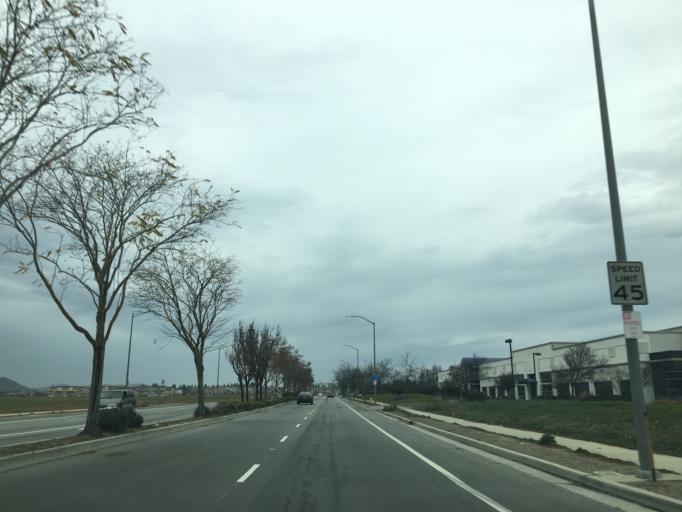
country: US
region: California
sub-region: Santa Clara County
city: Morgan Hill
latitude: 37.1404
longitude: -121.6552
